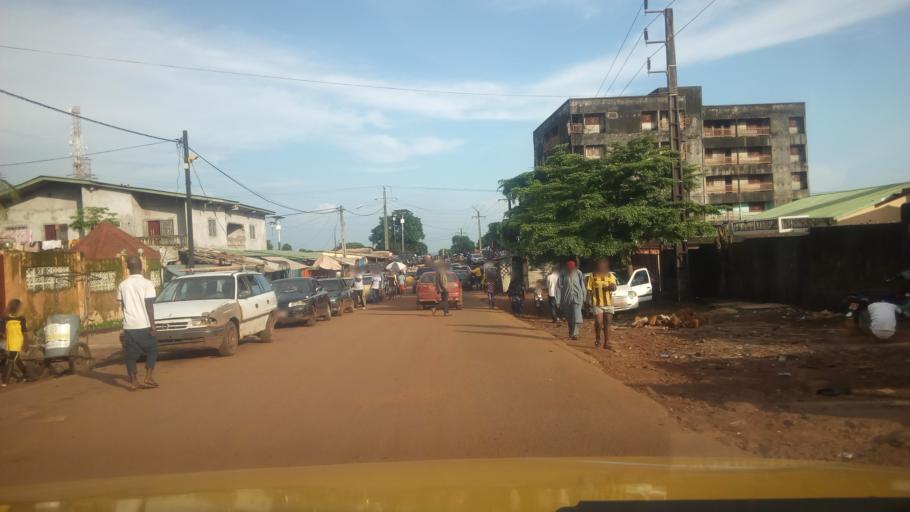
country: GN
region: Conakry
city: Conakry
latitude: 9.6161
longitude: -13.6073
